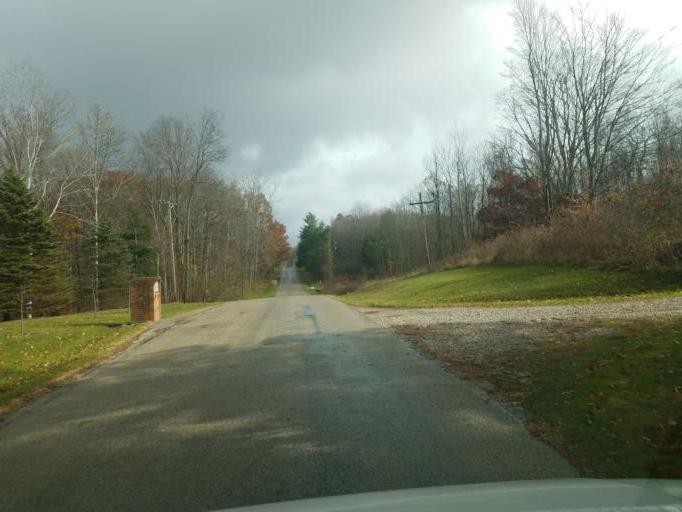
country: US
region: Ohio
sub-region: Richland County
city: Ontario
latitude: 40.7394
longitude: -82.6284
